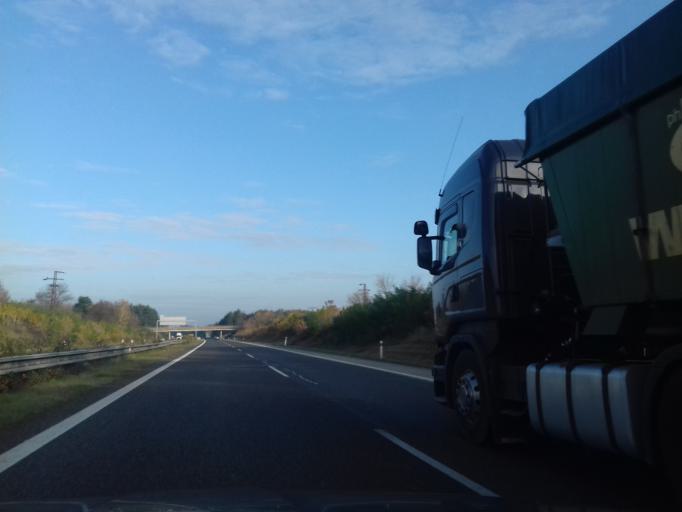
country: SK
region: Bratislavsky
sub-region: Okres Malacky
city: Malacky
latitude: 48.4388
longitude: 17.0431
